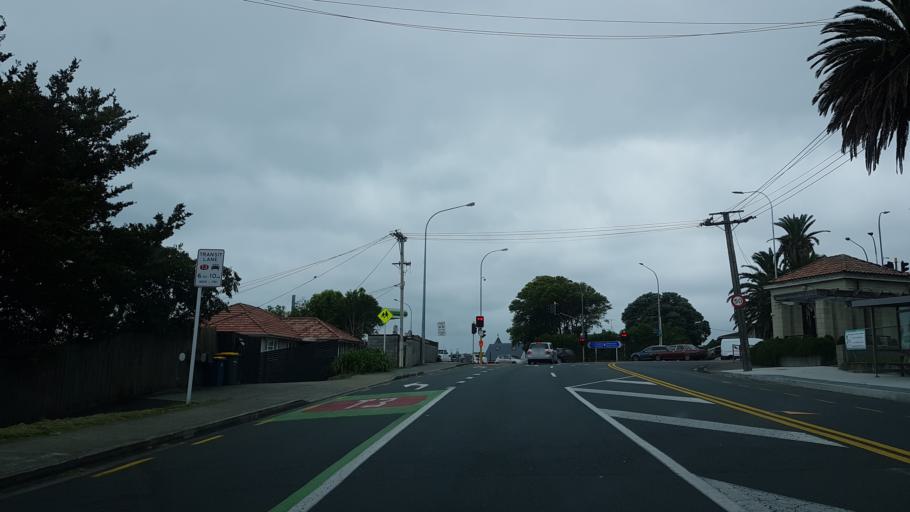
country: NZ
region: Auckland
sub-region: Auckland
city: North Shore
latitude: -36.8104
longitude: 174.7435
